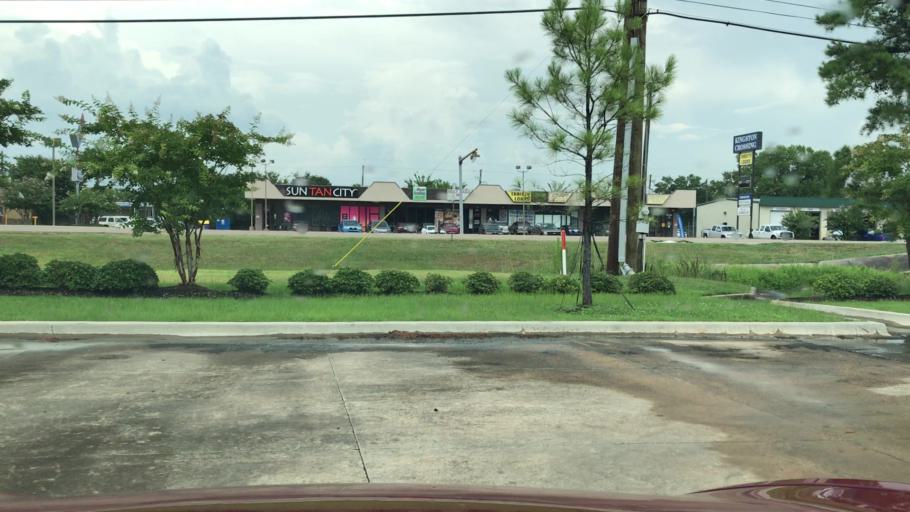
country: US
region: Louisiana
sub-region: Bossier Parish
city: Bossier City
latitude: 32.4010
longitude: -93.7795
